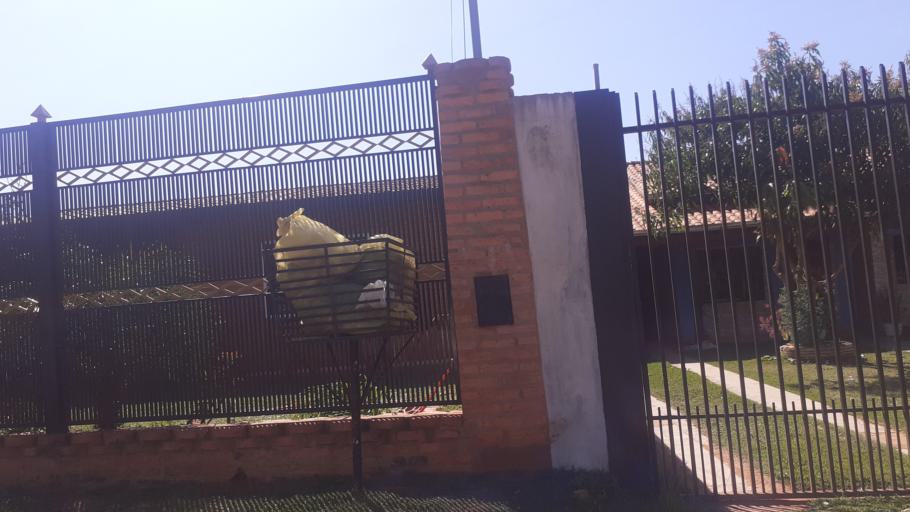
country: PY
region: Misiones
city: San Juan Bautista
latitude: -26.6670
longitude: -57.1261
